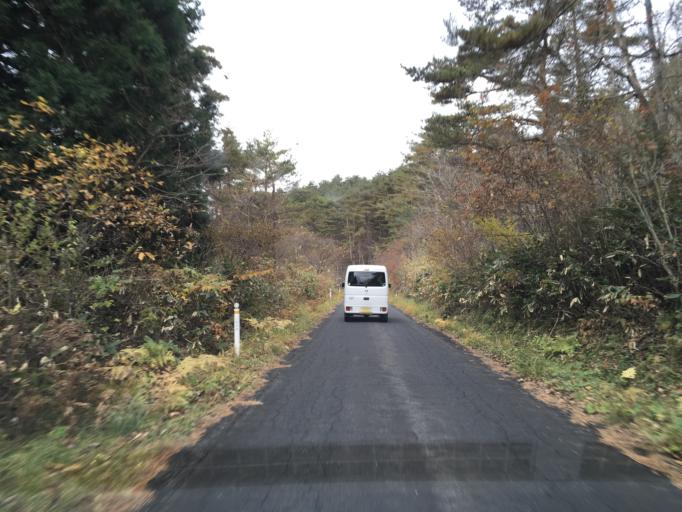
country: JP
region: Iwate
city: Mizusawa
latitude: 39.1273
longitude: 141.3146
